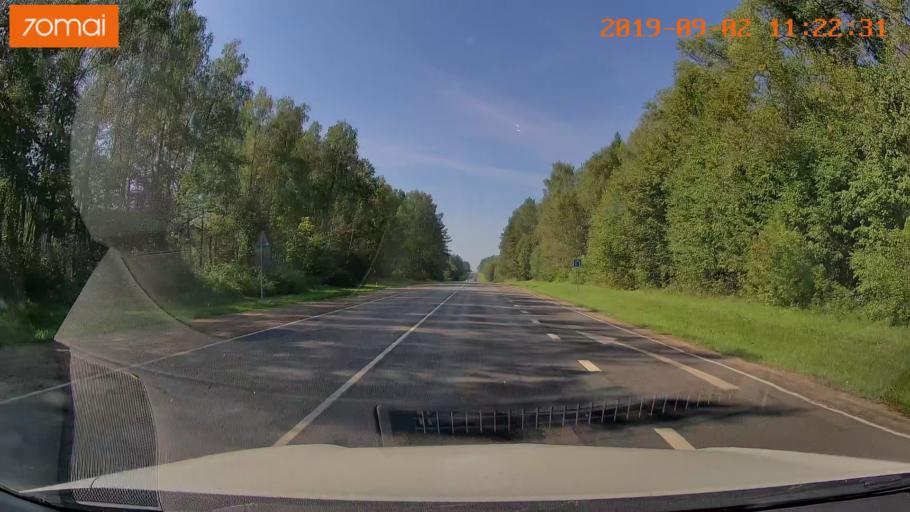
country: RU
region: Smolensk
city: Roslavl'
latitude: 54.0251
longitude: 33.0116
